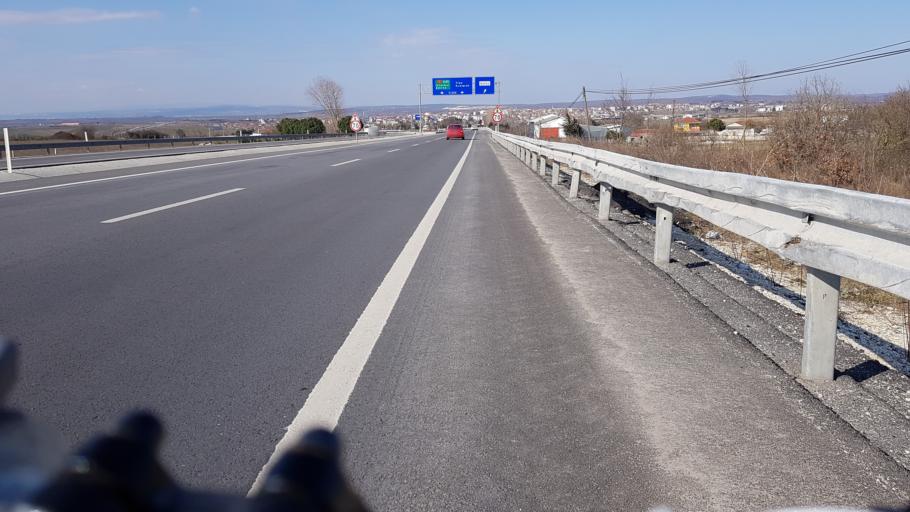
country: TR
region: Tekirdag
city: Saray
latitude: 41.4145
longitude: 27.9225
